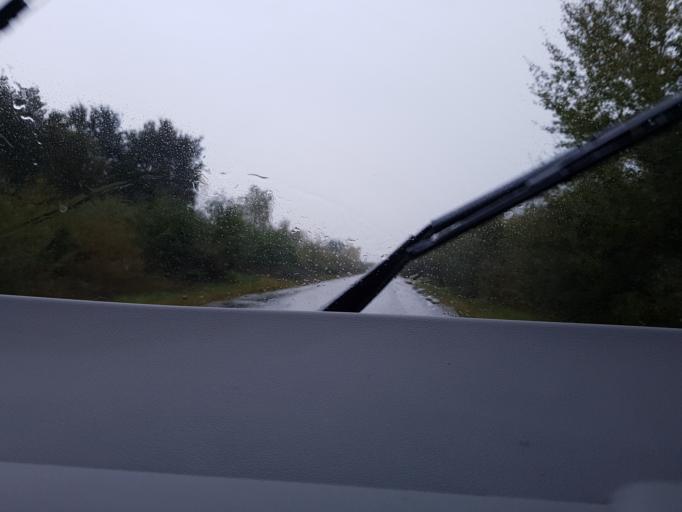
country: FR
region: Aquitaine
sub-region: Departement de la Gironde
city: Saint-Louis-de-Montferrand
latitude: 44.9480
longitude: -0.5201
